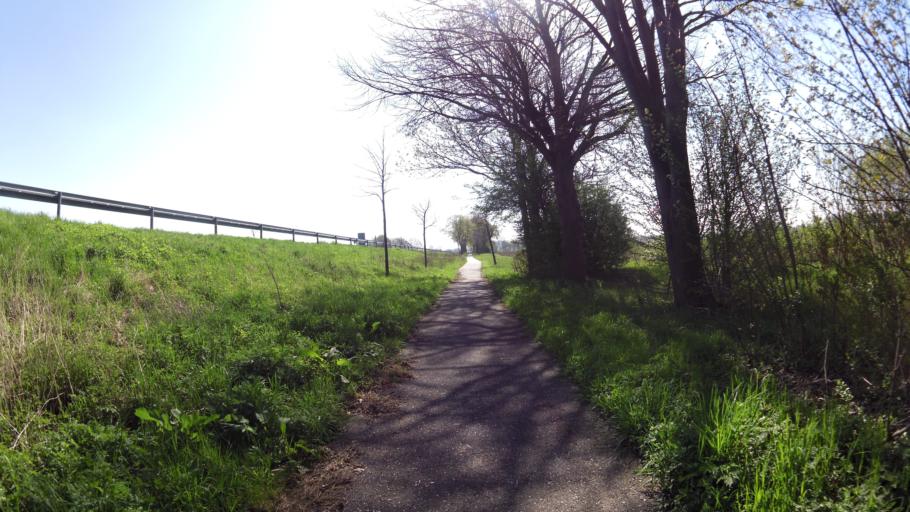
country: DE
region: North Rhine-Westphalia
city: Baesweiler
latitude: 50.9472
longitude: 6.1831
